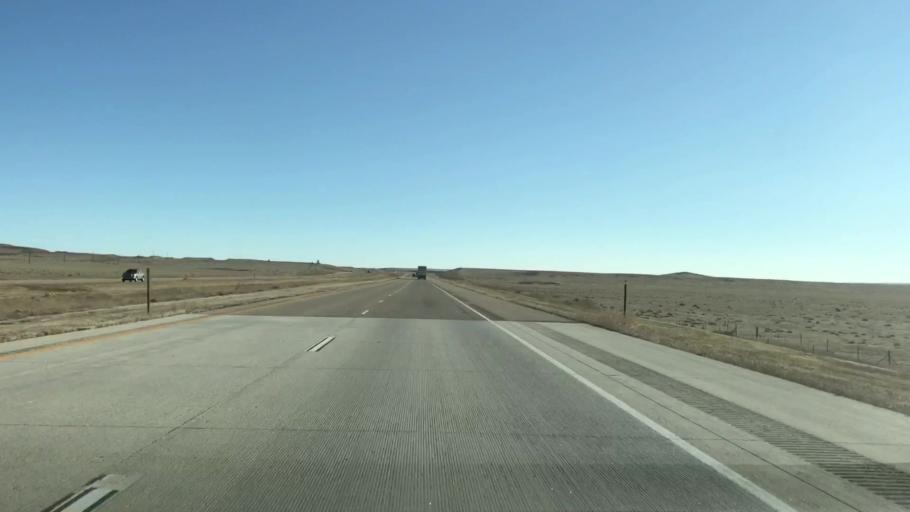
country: US
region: Colorado
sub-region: Lincoln County
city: Hugo
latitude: 39.2660
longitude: -103.5410
